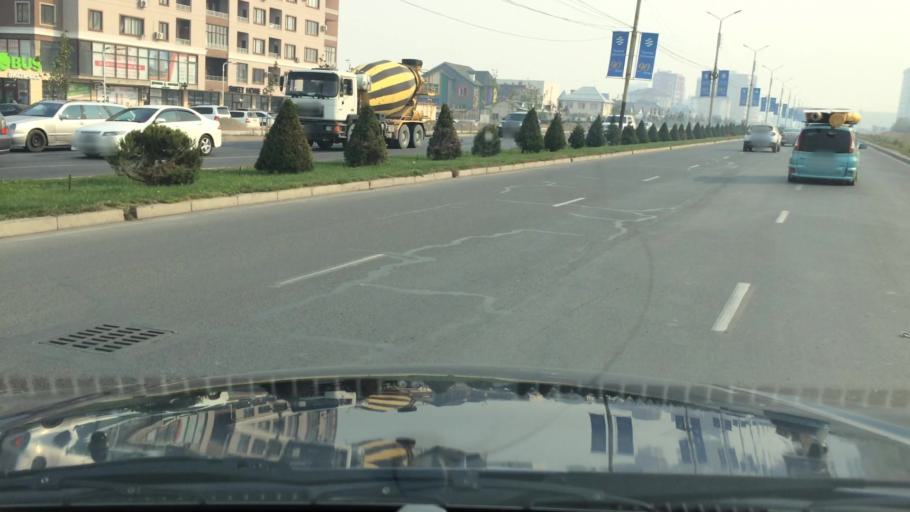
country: KG
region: Chuy
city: Bishkek
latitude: 42.8294
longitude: 74.5695
